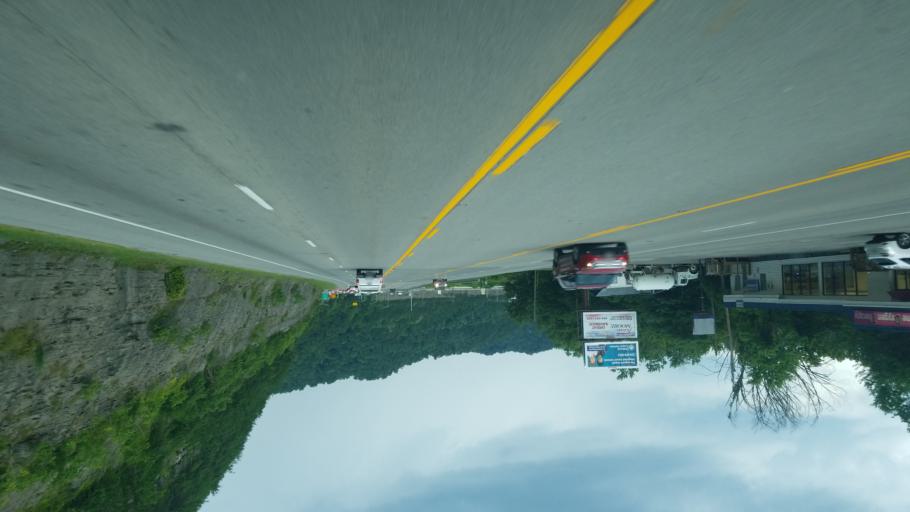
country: US
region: Kentucky
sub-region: Pike County
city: Pikeville
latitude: 37.4982
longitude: -82.5311
